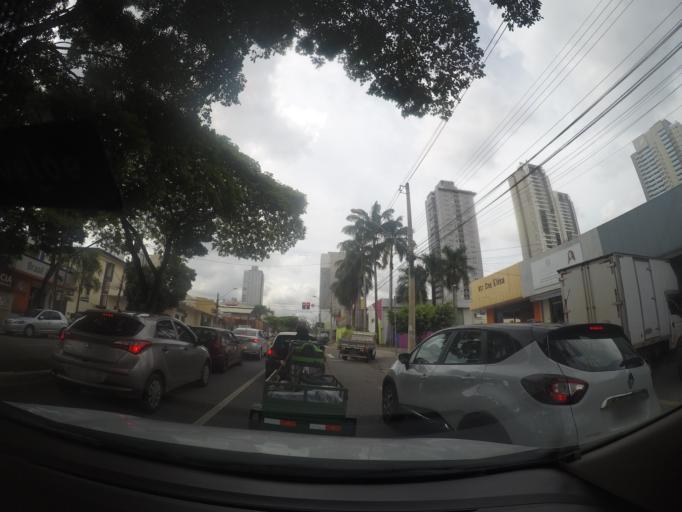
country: BR
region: Goias
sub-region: Goiania
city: Goiania
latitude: -16.7010
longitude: -49.2742
